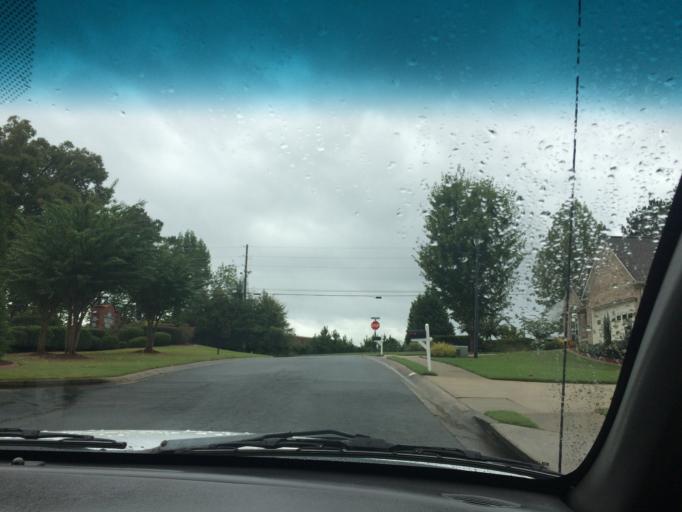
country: US
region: Georgia
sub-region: Cobb County
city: Acworth
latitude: 34.0558
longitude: -84.6478
